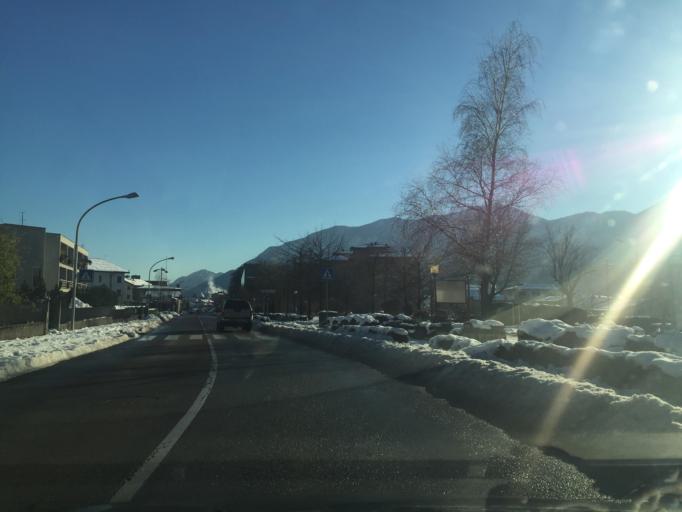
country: IT
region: Friuli Venezia Giulia
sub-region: Provincia di Udine
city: Tolmezzo
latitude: 46.4076
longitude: 13.0093
